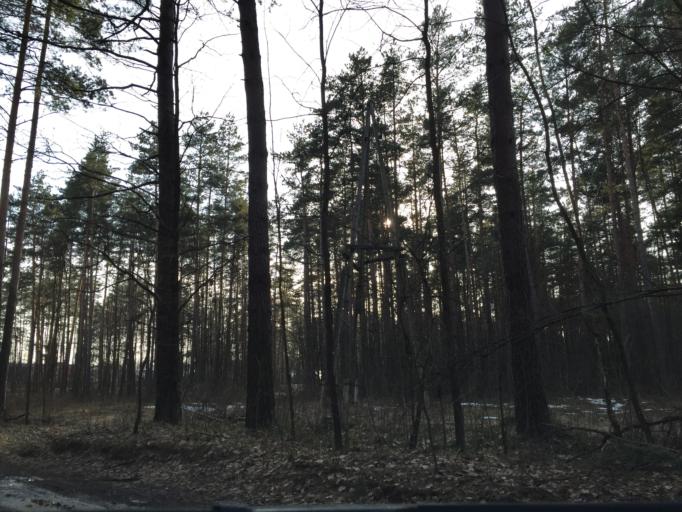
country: LV
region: Stopini
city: Ulbroka
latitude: 56.9459
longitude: 24.2890
